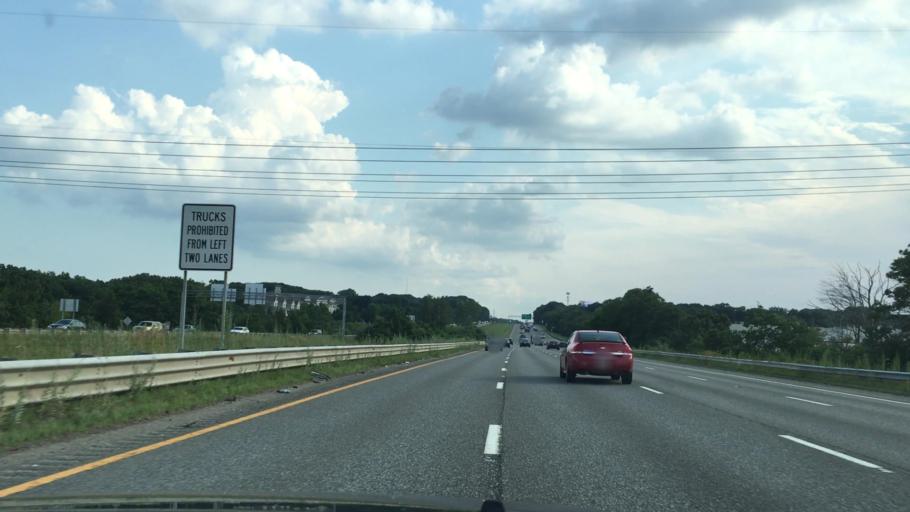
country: US
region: Massachusetts
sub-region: Essex County
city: Danvers
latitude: 42.5589
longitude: -70.9749
